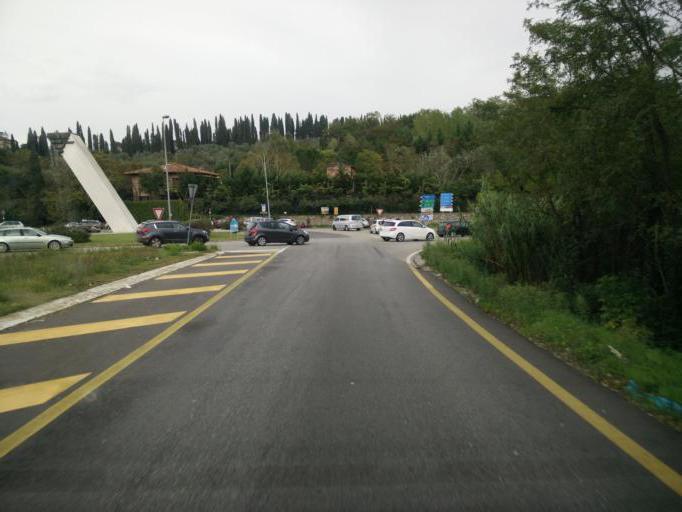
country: IT
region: Tuscany
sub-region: Province of Florence
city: Tavarnuzze
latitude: 43.7198
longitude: 11.2225
